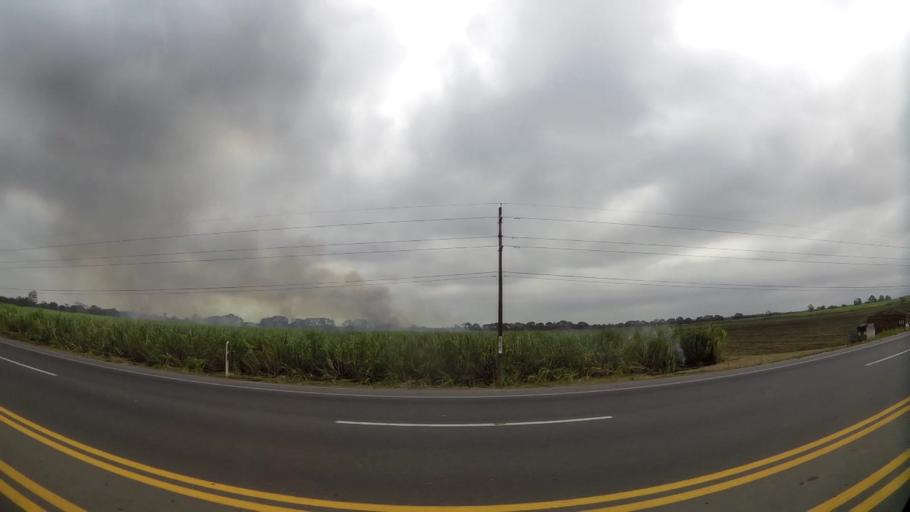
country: EC
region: Guayas
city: Yaguachi Nuevo
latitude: -2.2748
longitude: -79.6385
